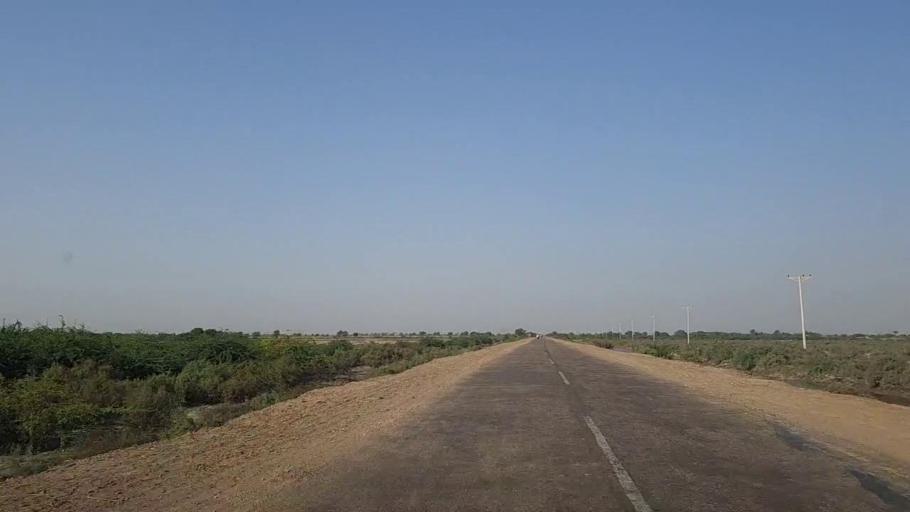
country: PK
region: Sindh
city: Mirpur Batoro
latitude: 24.6167
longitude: 68.4051
